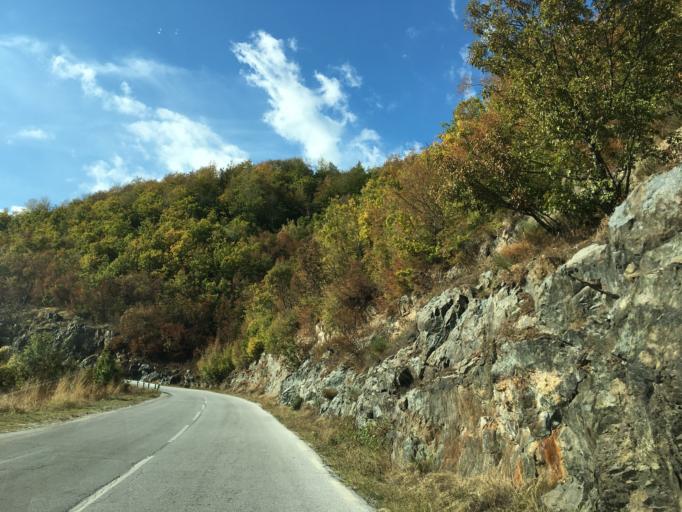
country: BG
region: Smolyan
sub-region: Obshtina Madan
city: Madan
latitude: 41.4513
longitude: 24.9846
